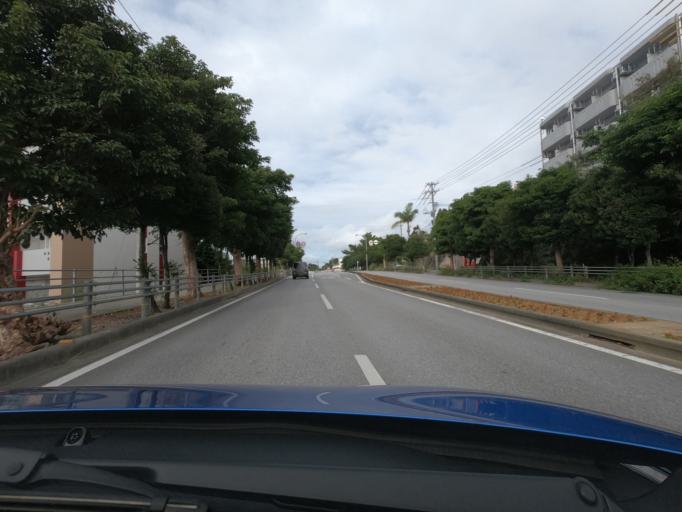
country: JP
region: Okinawa
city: Nago
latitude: 26.6726
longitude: 127.8899
